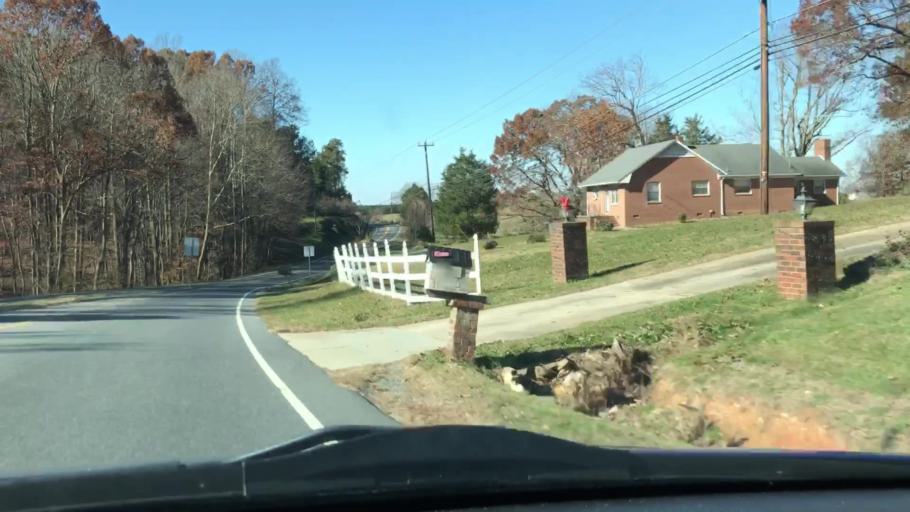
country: US
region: North Carolina
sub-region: Randolph County
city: Asheboro
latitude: 35.6818
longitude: -79.8491
